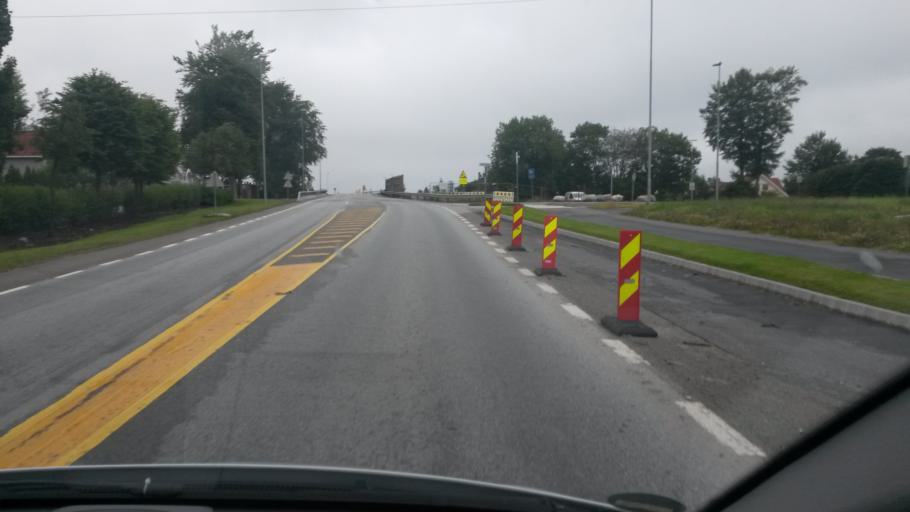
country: NO
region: Rogaland
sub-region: Sandnes
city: Sandnes
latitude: 58.8351
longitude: 5.7210
